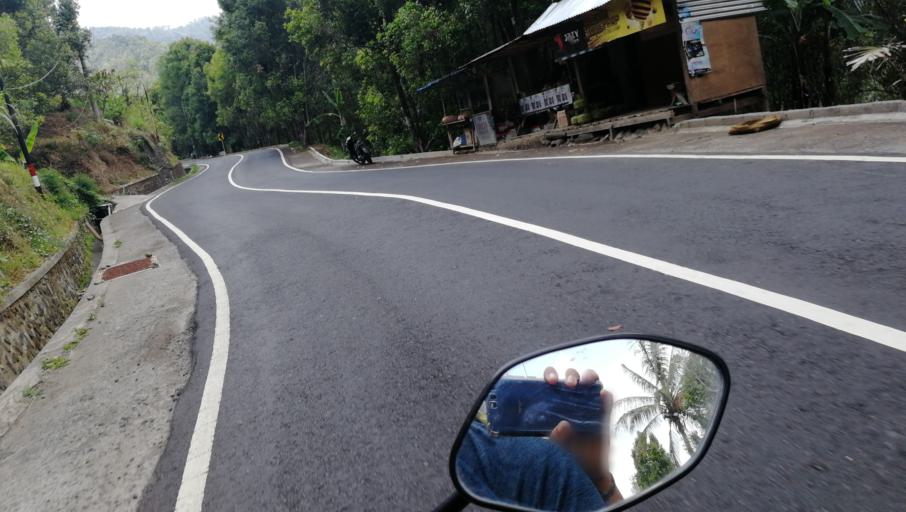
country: ID
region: Bali
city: Munduk
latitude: -8.2631
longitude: 115.0634
